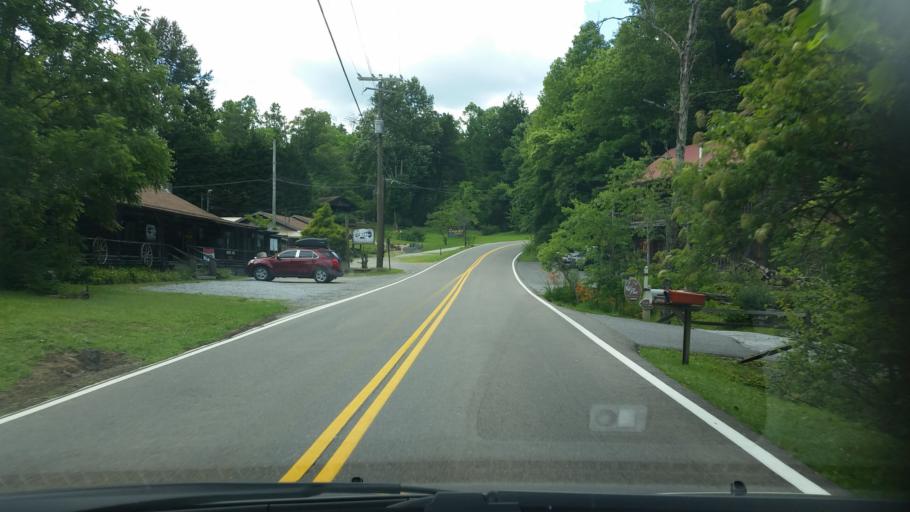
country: US
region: Tennessee
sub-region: Sevier County
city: Gatlinburg
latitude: 35.7517
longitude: -83.4358
